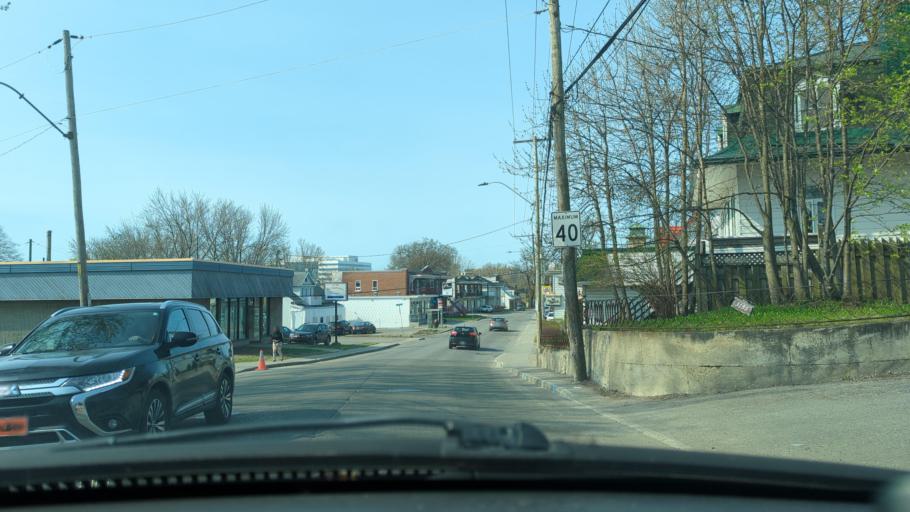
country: CA
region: Quebec
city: Quebec
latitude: 46.8508
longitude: -71.2105
